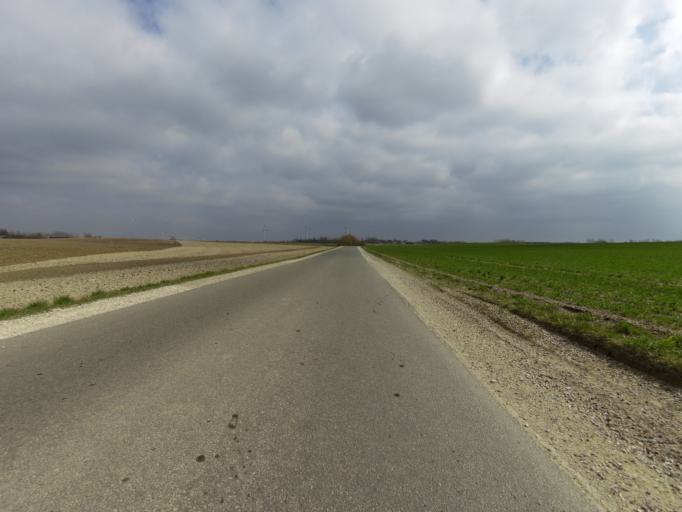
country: DK
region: Central Jutland
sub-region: Holstebro Kommune
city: Holstebro
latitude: 56.4345
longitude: 8.6738
